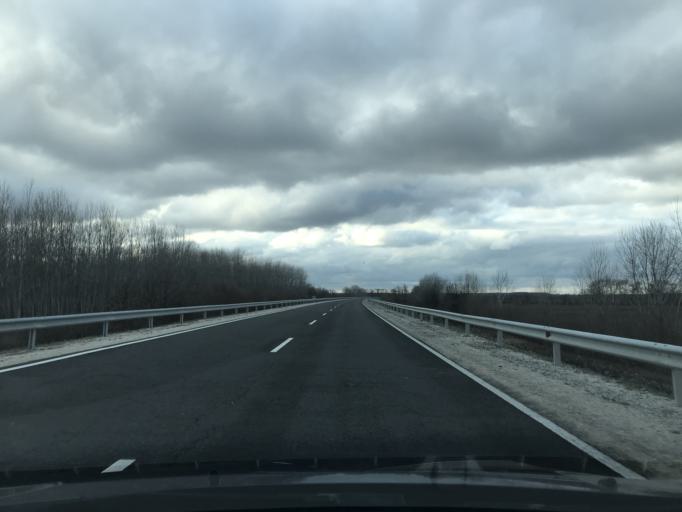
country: HU
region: Bacs-Kiskun
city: Dusnok
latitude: 46.3517
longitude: 18.9467
